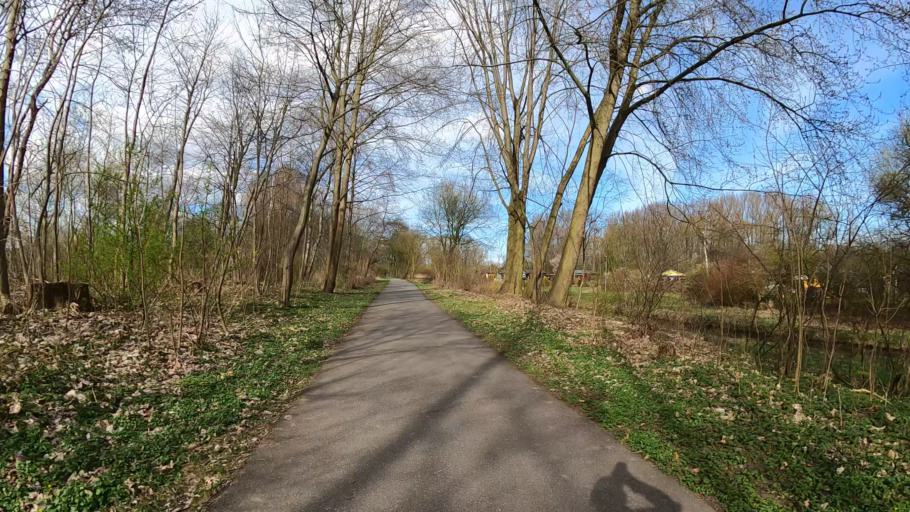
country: DE
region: Hamburg
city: Rothenburgsort
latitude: 53.4874
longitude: 10.0754
